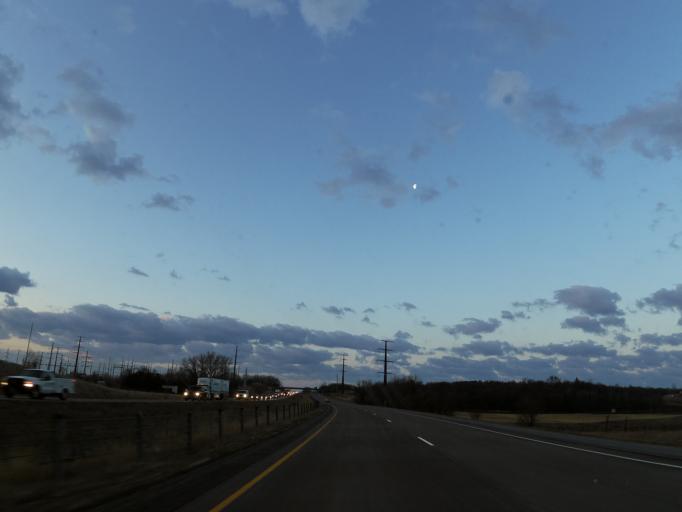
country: US
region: Minnesota
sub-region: Scott County
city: Elko New Market
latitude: 44.6013
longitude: -93.2981
